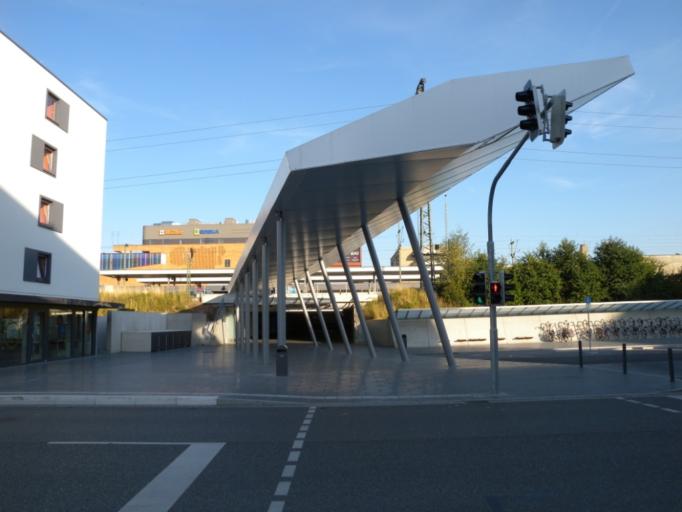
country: DE
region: Baden-Wuerttemberg
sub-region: Regierungsbezirk Stuttgart
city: Boeblingen
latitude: 48.6886
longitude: 9.0040
